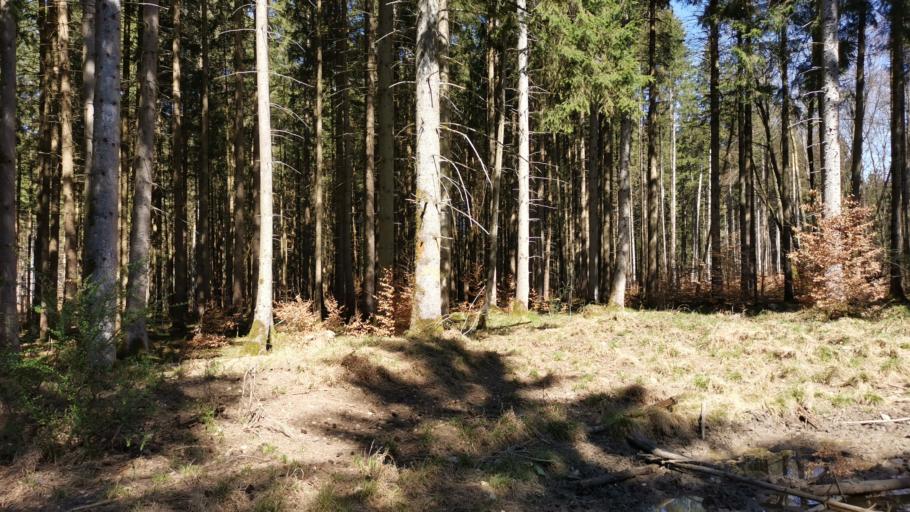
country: DE
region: Bavaria
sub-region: Upper Bavaria
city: Pullach im Isartal
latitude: 48.0685
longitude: 11.4933
